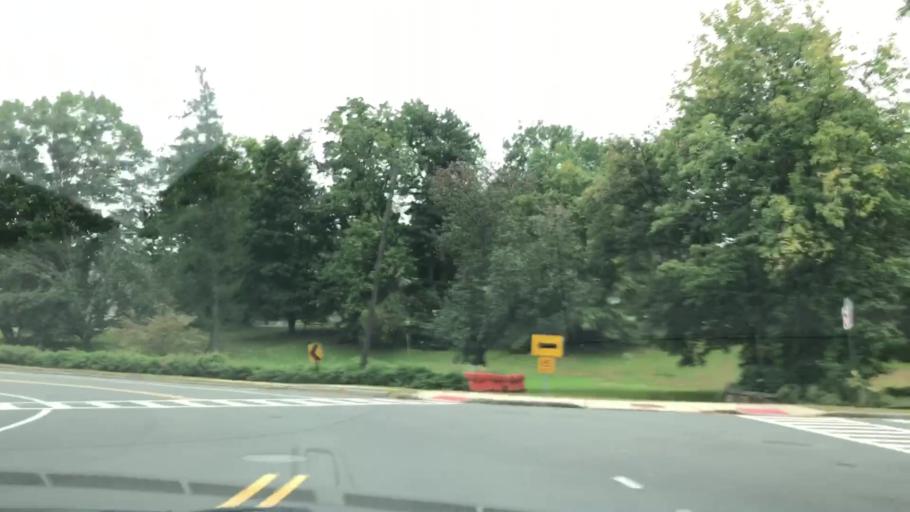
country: US
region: New Jersey
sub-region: Essex County
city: Glen Ridge
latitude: 40.8031
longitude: -74.2193
